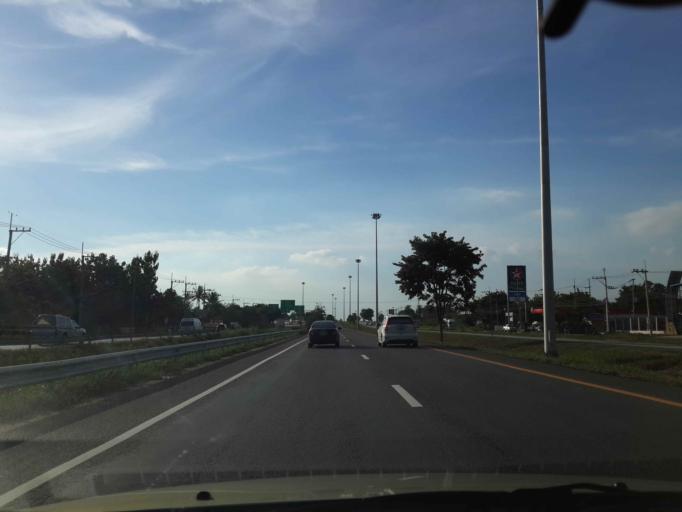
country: TH
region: Chon Buri
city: Bang Lamung
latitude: 12.9592
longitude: 100.9842
